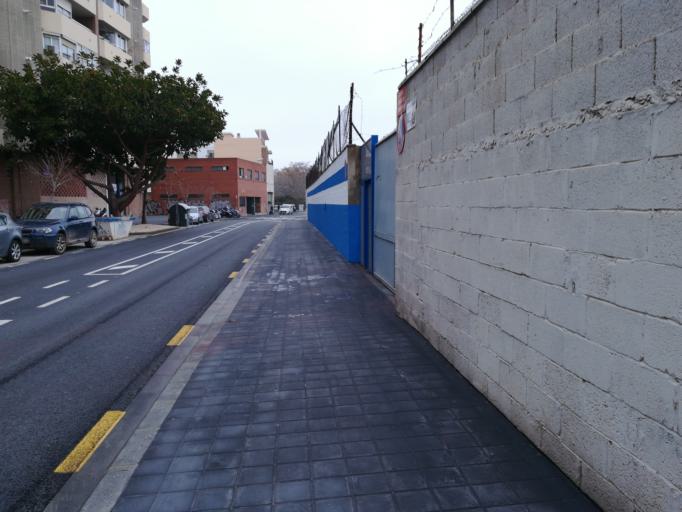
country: ES
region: Valencia
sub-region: Provincia de Valencia
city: Mislata
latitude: 39.4880
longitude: -0.4013
